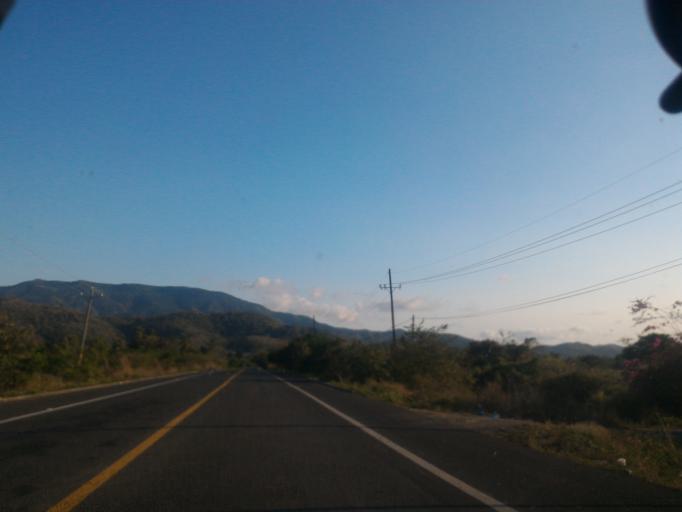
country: MX
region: Michoacan
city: Coahuayana Viejo
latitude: 18.6655
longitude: -103.6713
